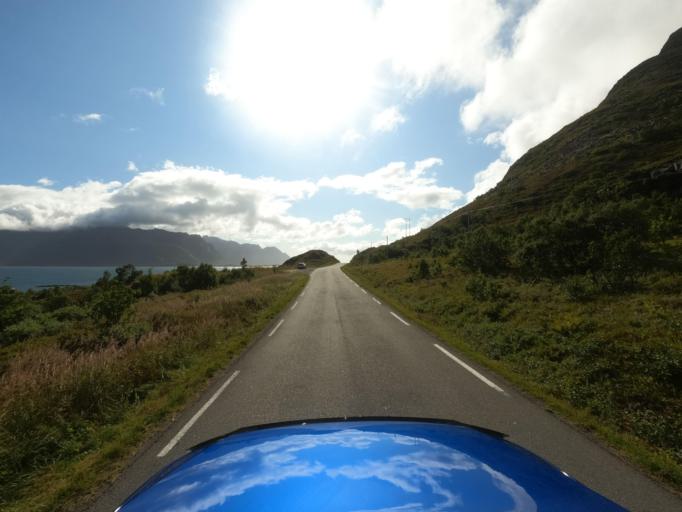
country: NO
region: Nordland
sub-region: Vagan
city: Kabelvag
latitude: 68.2606
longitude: 14.1638
